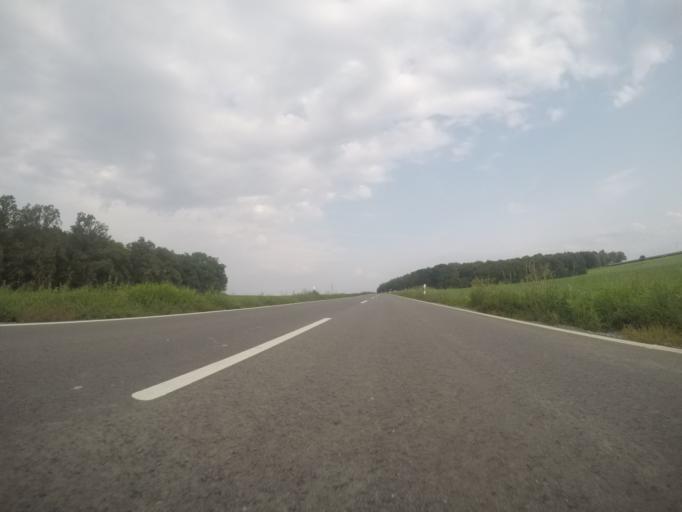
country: DE
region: Baden-Wuerttemberg
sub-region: Regierungsbezirk Stuttgart
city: Eberdingen
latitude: 48.8651
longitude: 8.9861
